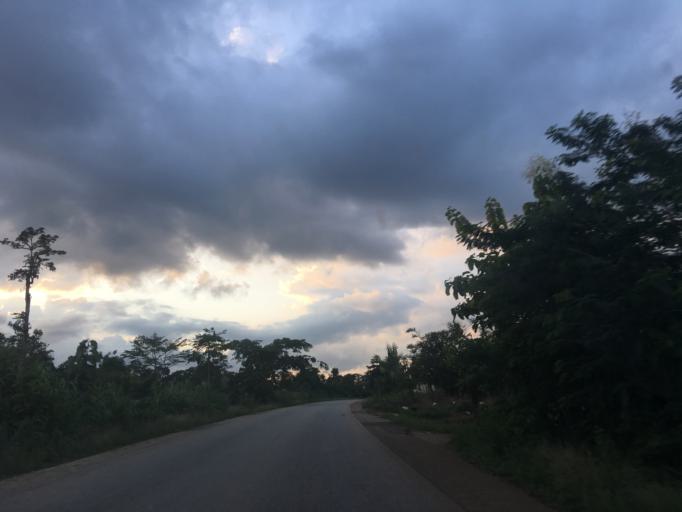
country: GH
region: Western
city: Bibiani
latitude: 6.7394
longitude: -2.5025
